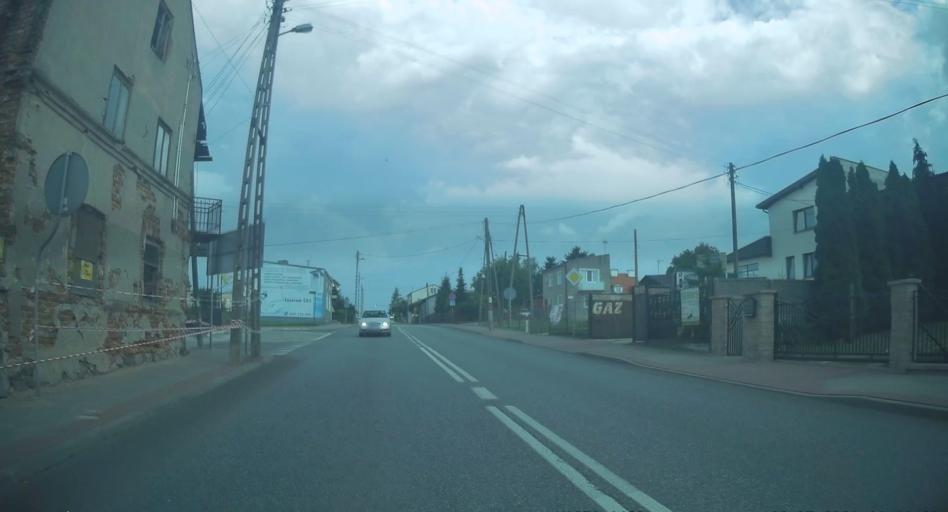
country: PL
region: Lodz Voivodeship
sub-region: Powiat brzezinski
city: Jezow
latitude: 51.8133
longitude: 19.9703
